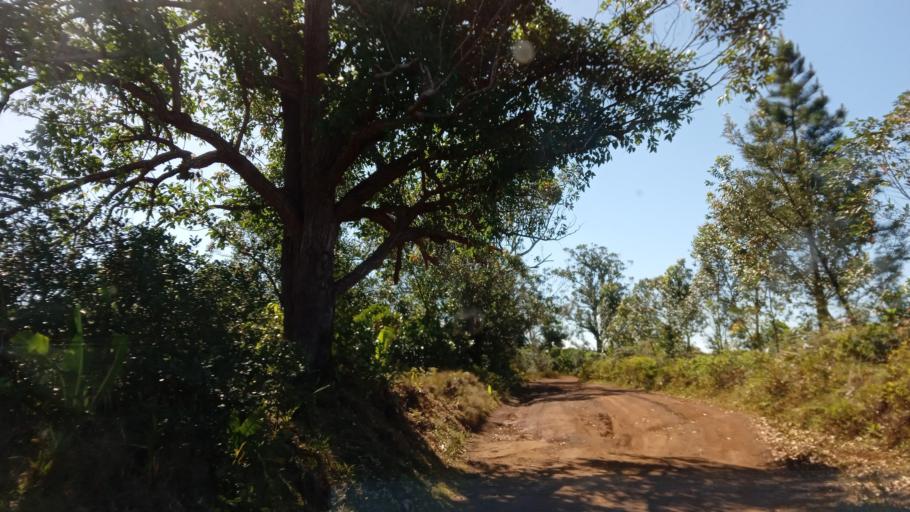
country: MG
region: Atsimo-Atsinanana
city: Vohipaho
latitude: -23.6646
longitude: 47.5796
